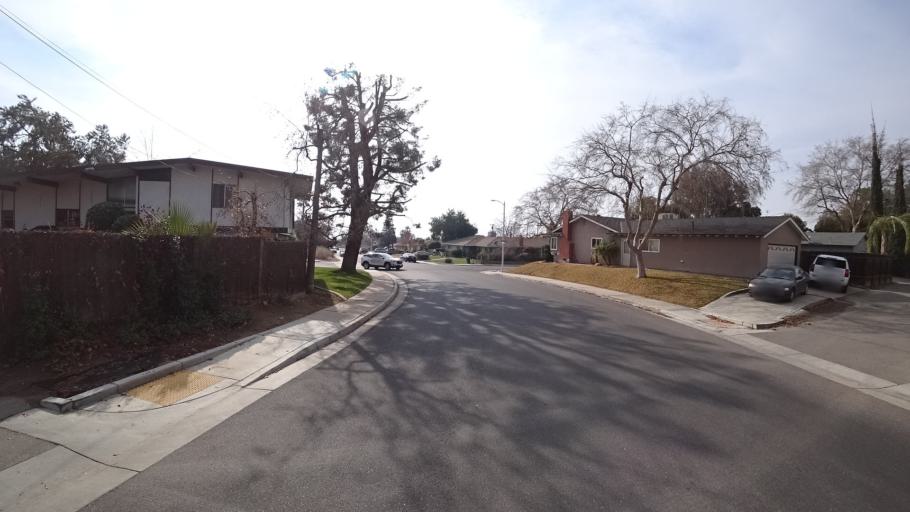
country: US
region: California
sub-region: Kern County
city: Oildale
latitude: 35.4046
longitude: -118.9525
